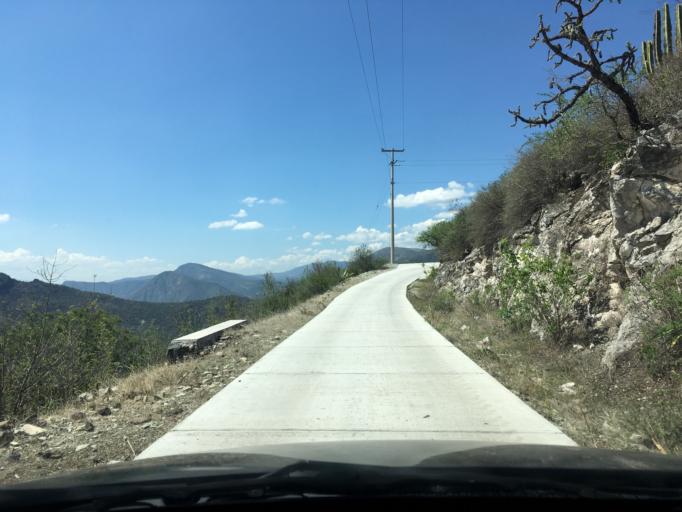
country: MX
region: Hidalgo
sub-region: Metztitlan
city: Fontezuelas
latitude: 20.6357
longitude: -98.8416
